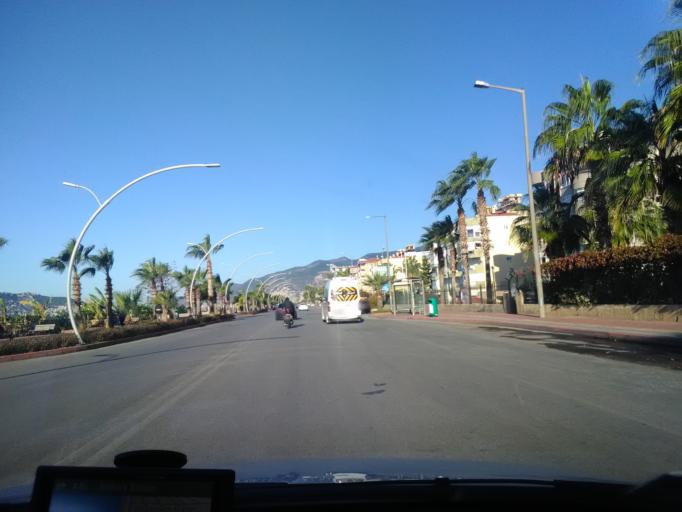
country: TR
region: Antalya
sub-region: Alanya
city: Alanya
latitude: 36.5274
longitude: 32.0471
